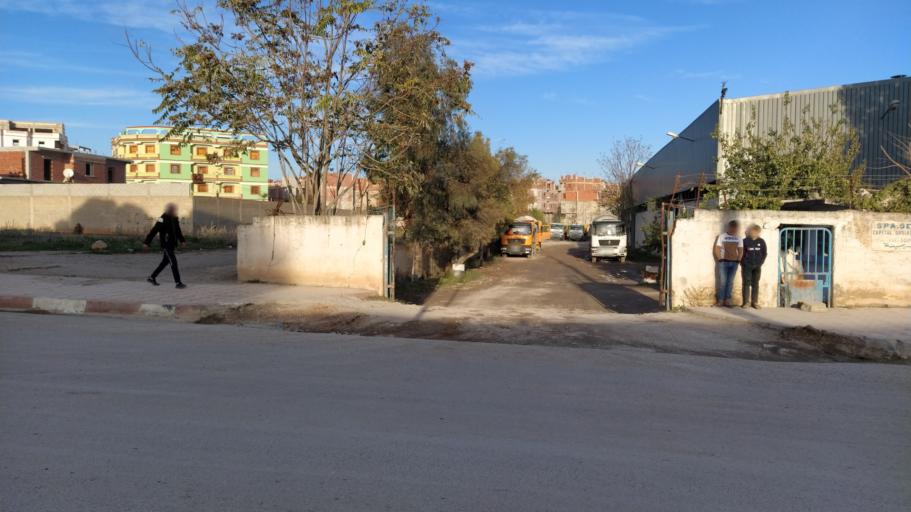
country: DZ
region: Constantine
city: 'Ain Abid
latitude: 36.2354
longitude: 6.9421
